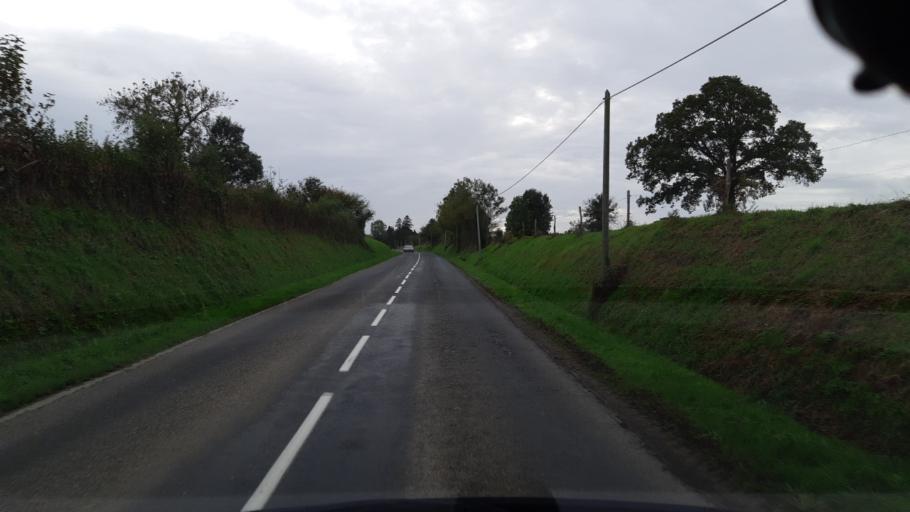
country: FR
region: Lower Normandy
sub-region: Departement de la Manche
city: Percy
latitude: 48.9992
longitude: -1.1948
